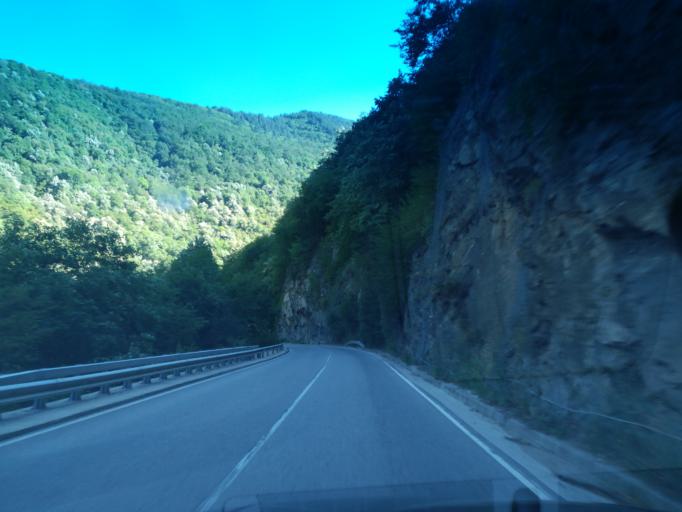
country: BG
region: Plovdiv
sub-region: Obshtina Luki
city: Luki
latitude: 41.9227
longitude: 24.8267
